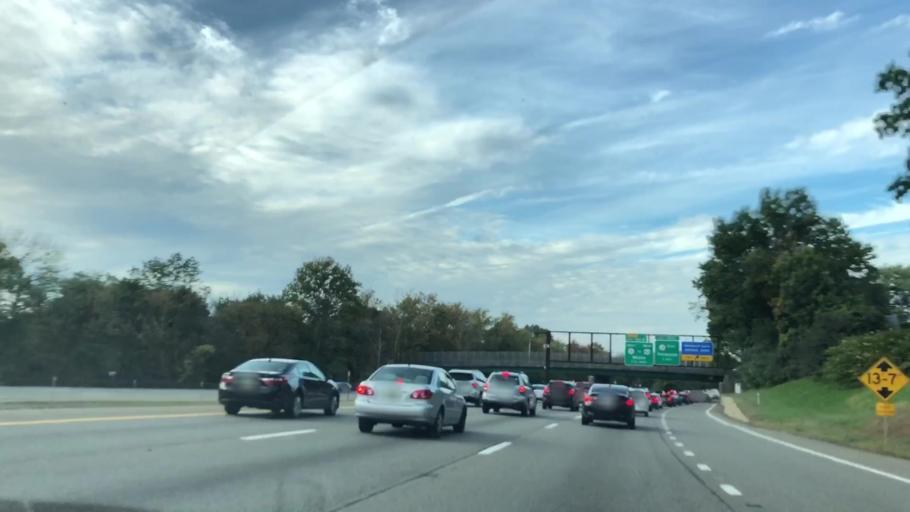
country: US
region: New Jersey
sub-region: Essex County
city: Brookdale
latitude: 40.8322
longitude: -74.1786
